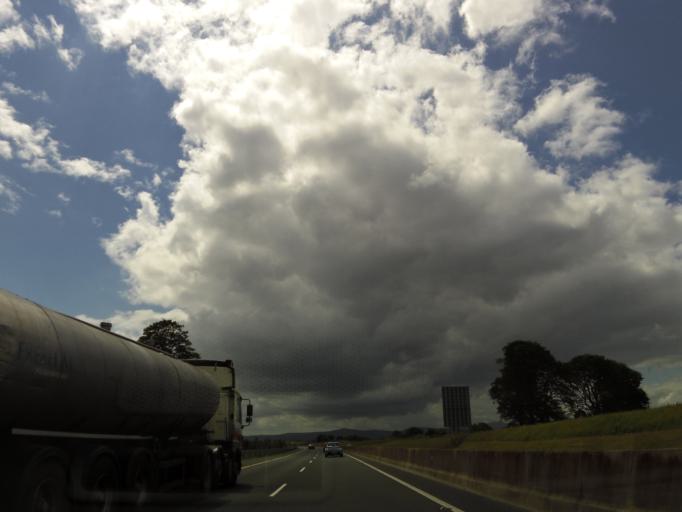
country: IE
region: Munster
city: Cashel
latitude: 52.4882
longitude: -7.9014
